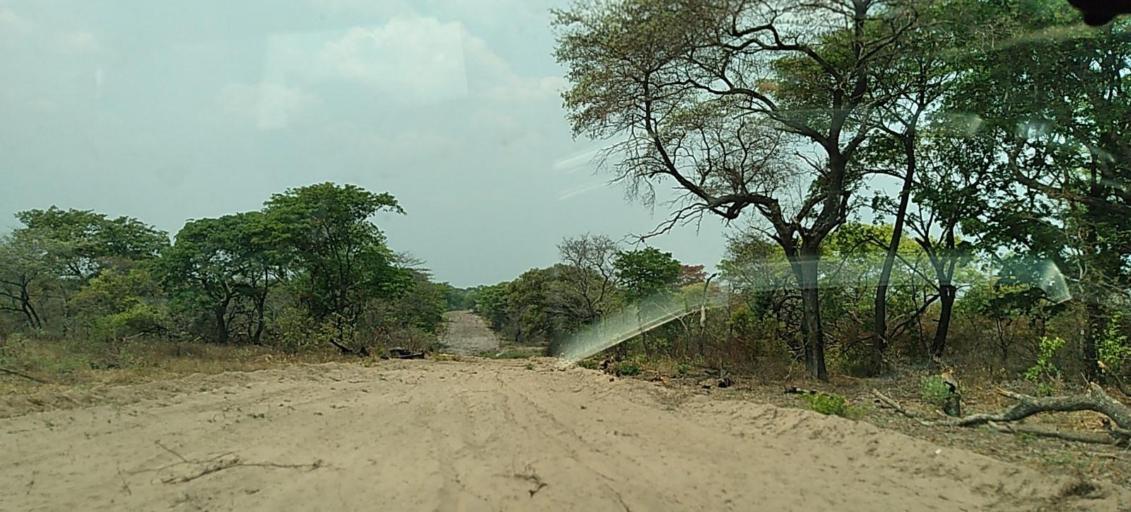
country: ZM
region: Western
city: Lukulu
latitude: -14.0035
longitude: 23.5876
